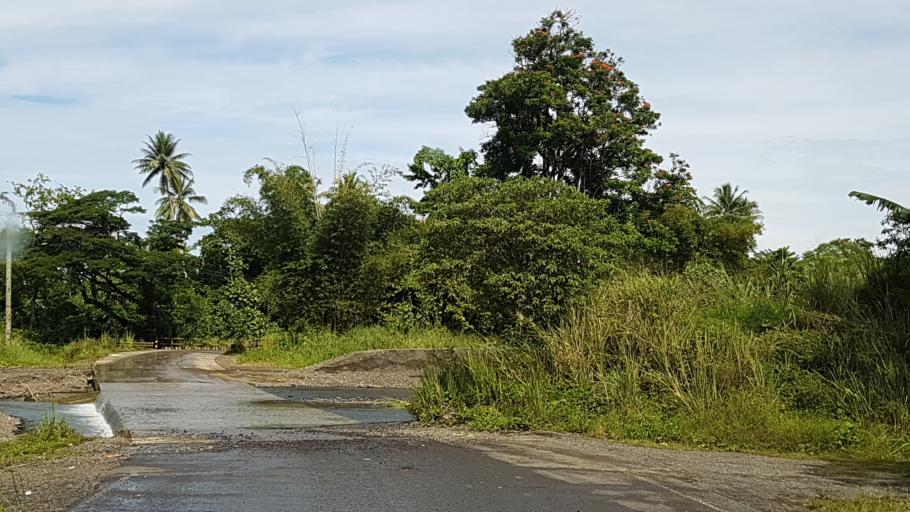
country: PG
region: Milne Bay
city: Alotau
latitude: -10.3233
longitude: 150.4801
